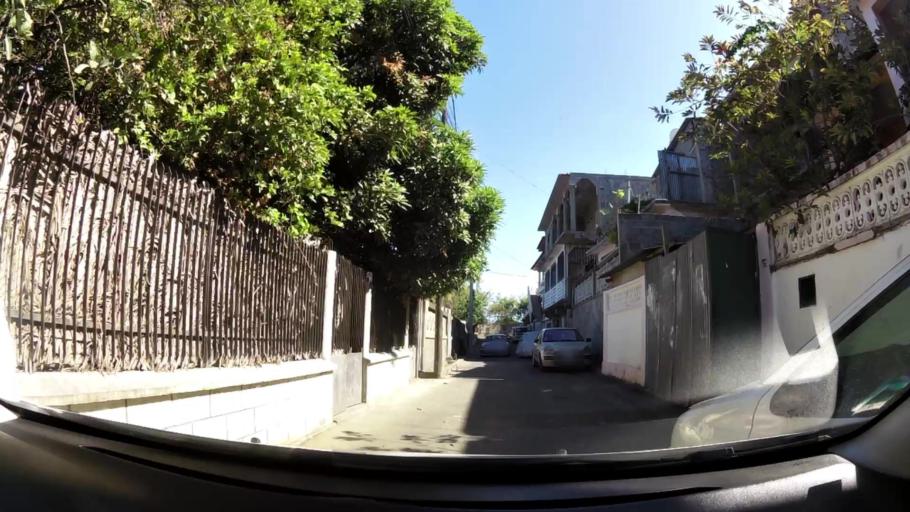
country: YT
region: Pamandzi
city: Pamandzi
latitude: -12.7836
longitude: 45.2786
